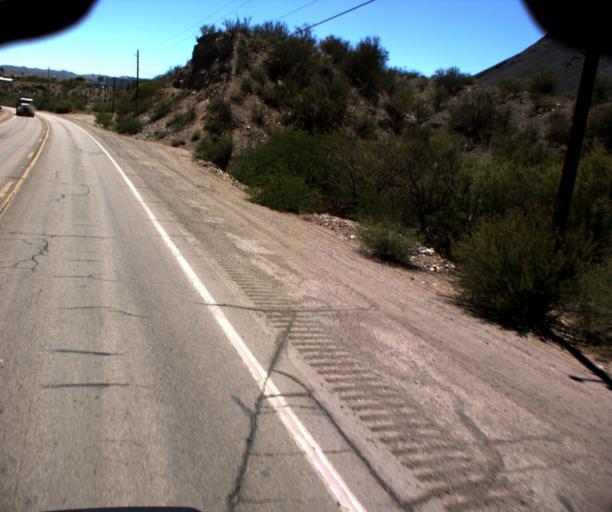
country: US
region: Arizona
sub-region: Pinal County
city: Kearny
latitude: 32.9992
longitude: -110.7678
